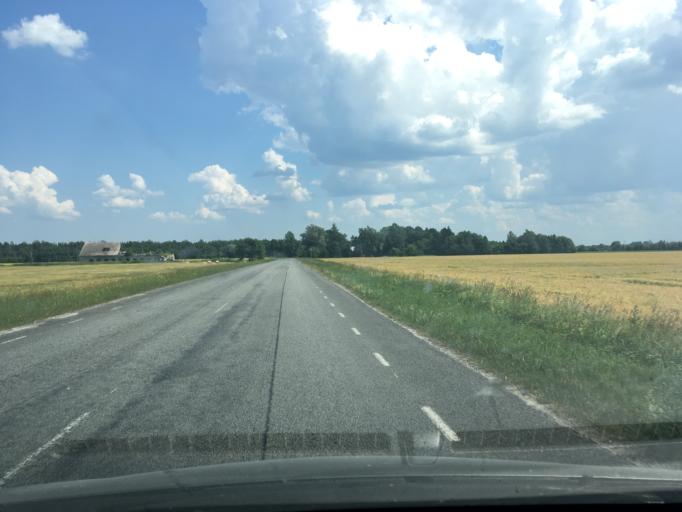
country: EE
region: Raplamaa
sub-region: Maerjamaa vald
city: Marjamaa
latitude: 58.7316
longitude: 24.2962
